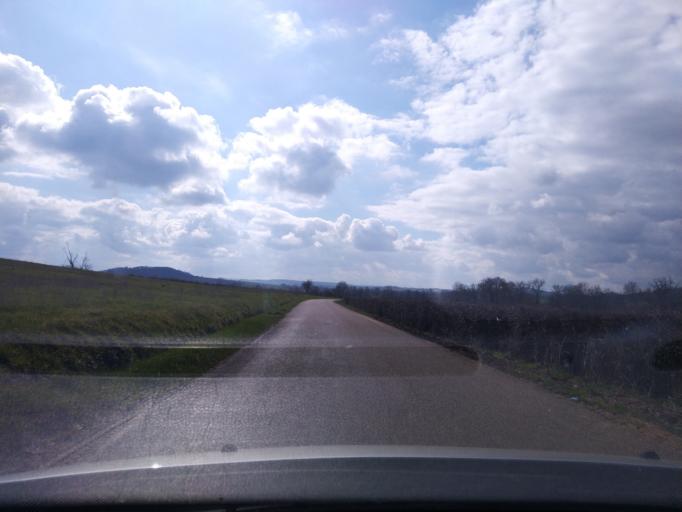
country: FR
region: Bourgogne
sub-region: Departement de l'Yonne
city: Avallon
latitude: 47.5554
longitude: 4.0577
